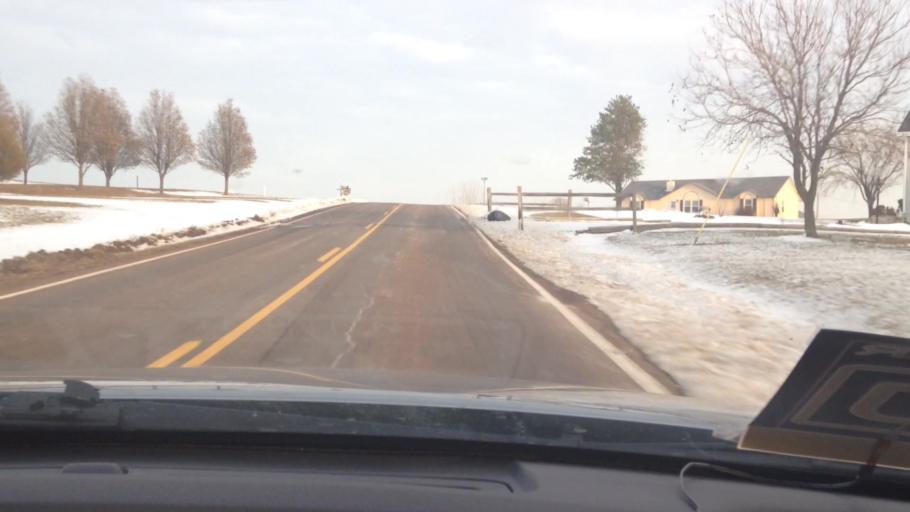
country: US
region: Kansas
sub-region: Leavenworth County
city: Lansing
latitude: 39.2304
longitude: -94.9647
